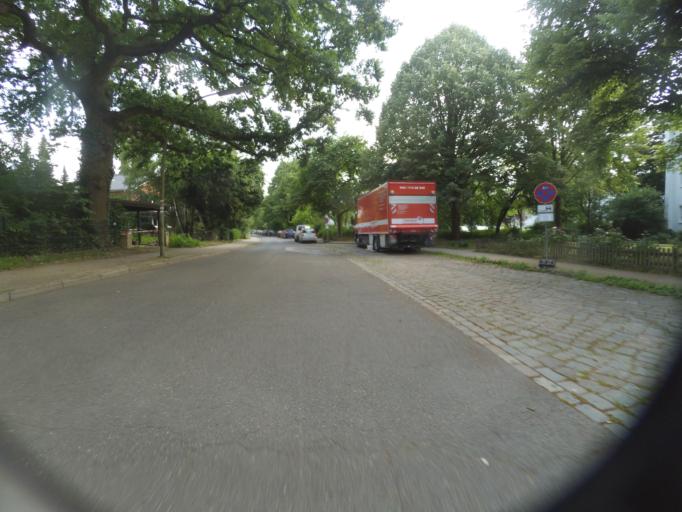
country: DE
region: Hamburg
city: Eidelstedt
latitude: 53.5690
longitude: 9.8703
